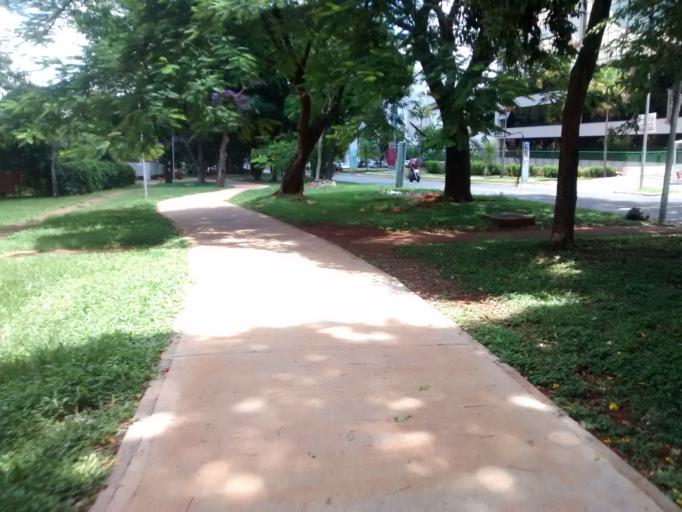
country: BR
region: Federal District
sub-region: Brasilia
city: Brasilia
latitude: -15.8128
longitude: -47.9111
